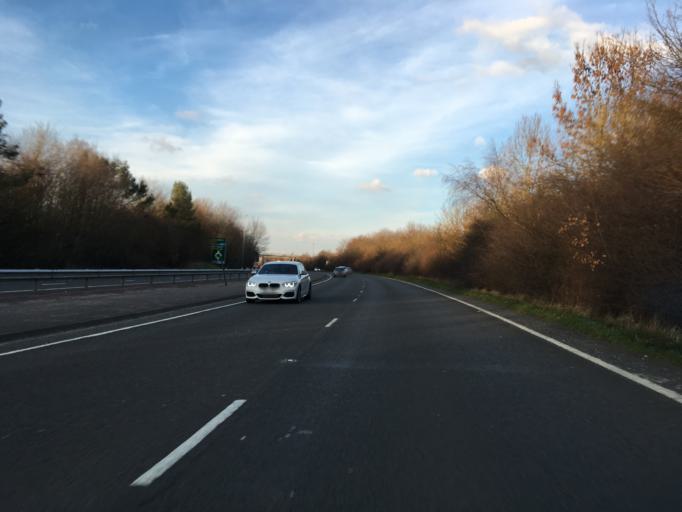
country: GB
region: England
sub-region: Borough of Stockport
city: Cheadle Hulme
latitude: 53.3449
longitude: -2.1997
